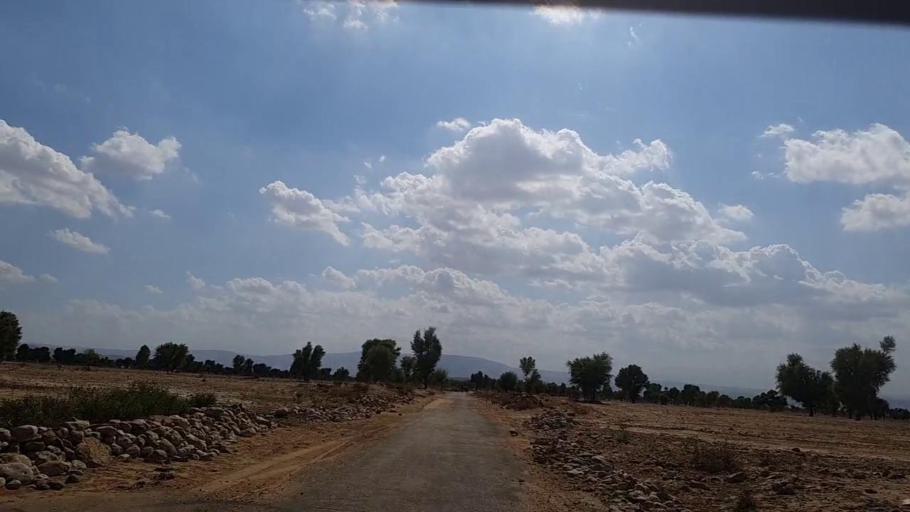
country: PK
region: Sindh
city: Johi
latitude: 26.5217
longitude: 67.4794
